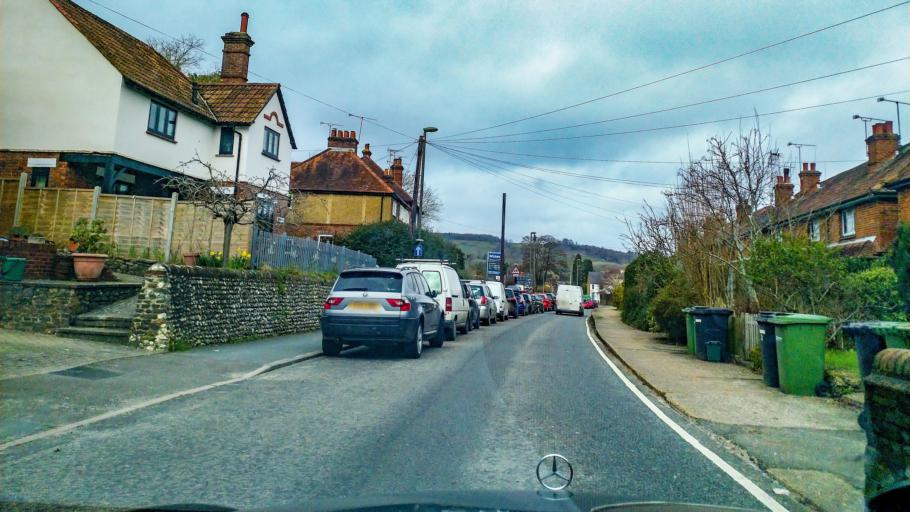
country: GB
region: England
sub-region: Surrey
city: Dorking
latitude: 51.2275
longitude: -0.3365
